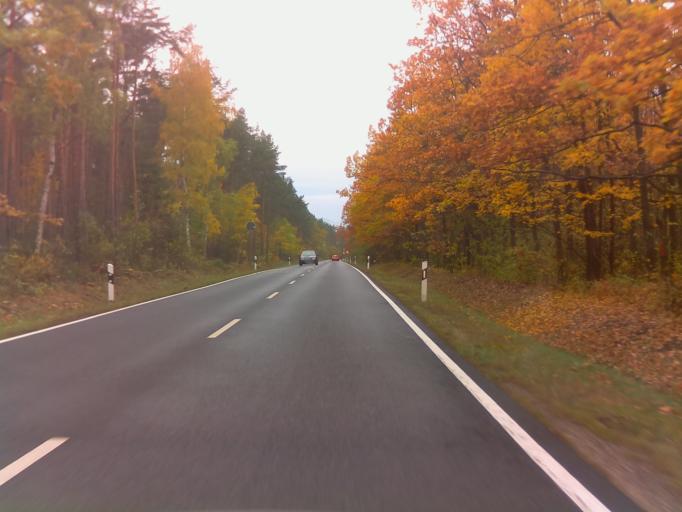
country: DE
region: Thuringia
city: Behringen
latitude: 50.7970
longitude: 11.0415
